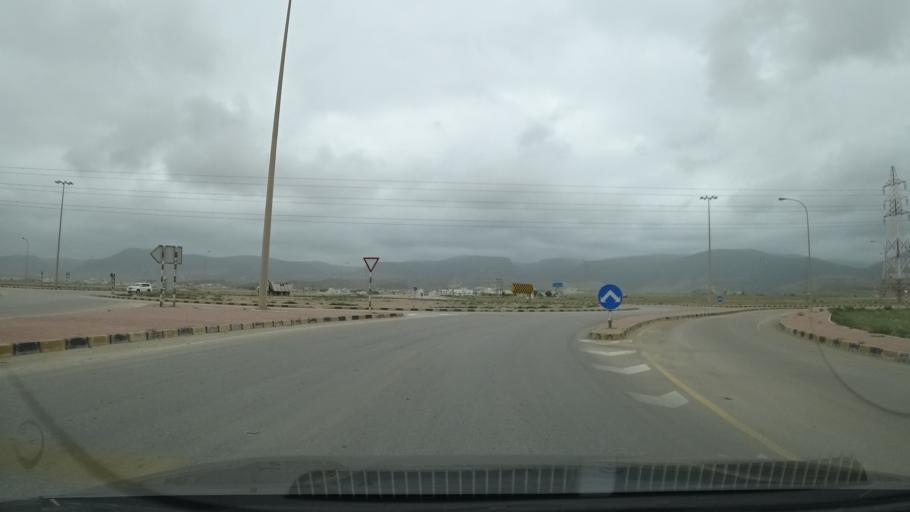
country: OM
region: Zufar
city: Salalah
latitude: 17.1026
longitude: 54.2166
